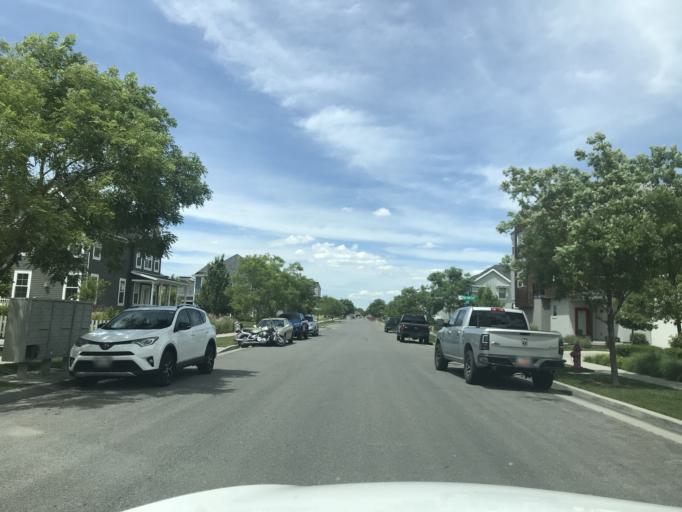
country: US
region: Utah
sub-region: Salt Lake County
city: South Jordan Heights
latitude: 40.5629
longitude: -111.9998
